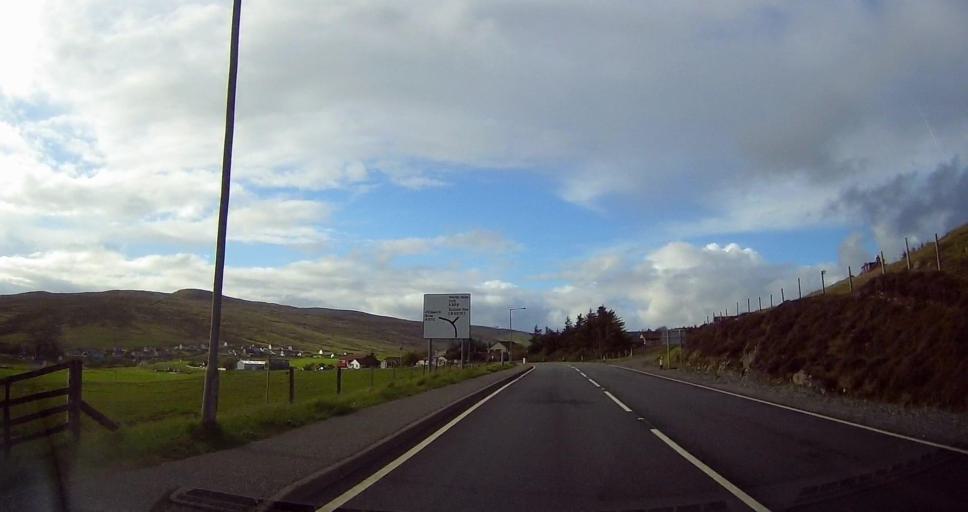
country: GB
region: Scotland
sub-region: Shetland Islands
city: Lerwick
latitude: 60.3531
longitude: -1.2612
